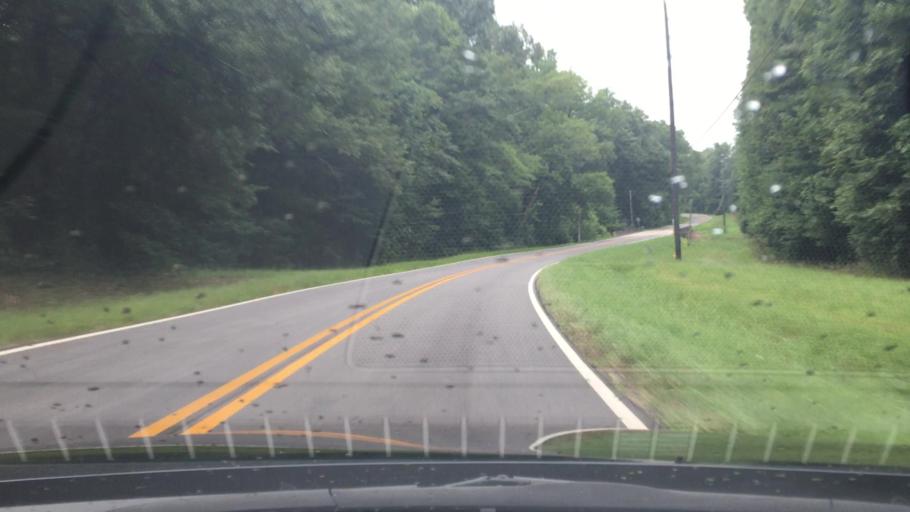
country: US
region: Georgia
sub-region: Spalding County
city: Experiment
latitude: 33.2789
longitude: -84.3820
